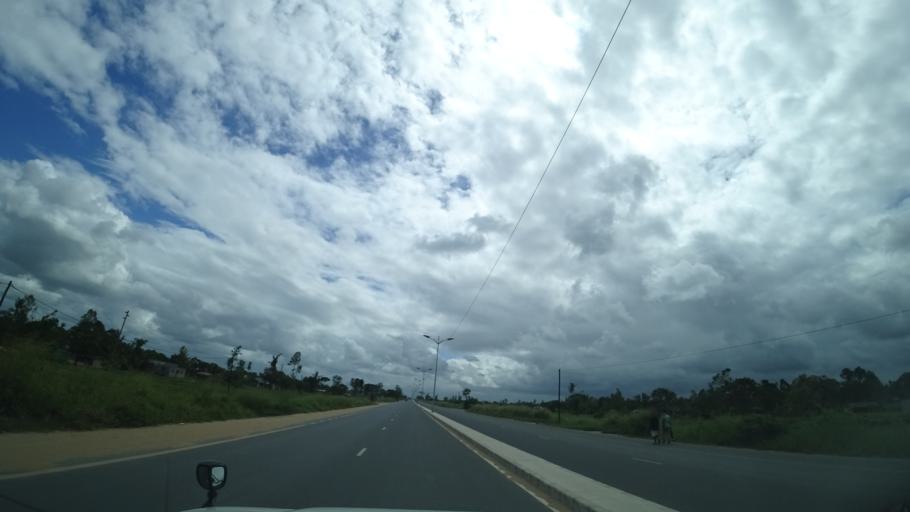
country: MZ
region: Sofala
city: Dondo
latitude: -19.5998
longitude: 34.7406
